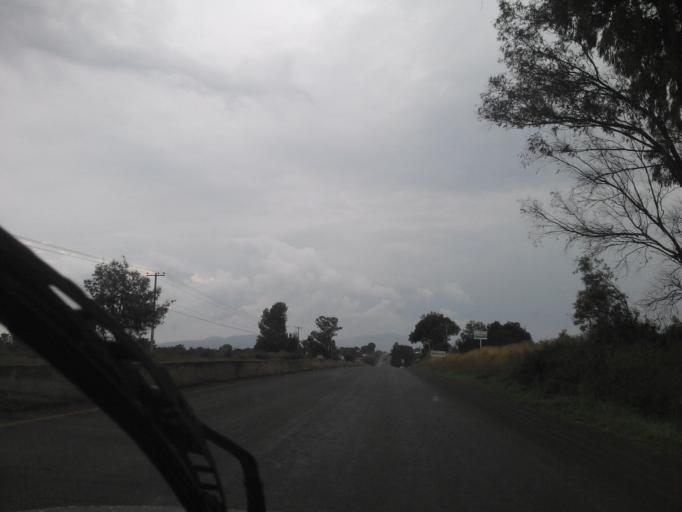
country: MX
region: Jalisco
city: Arandas
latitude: 20.7159
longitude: -102.4324
